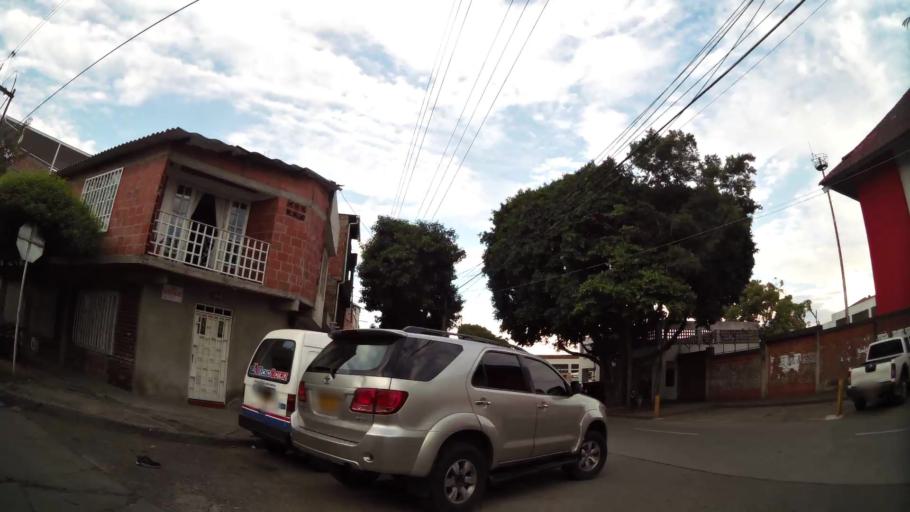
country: CO
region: Valle del Cauca
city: Cali
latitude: 3.4559
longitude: -76.5172
